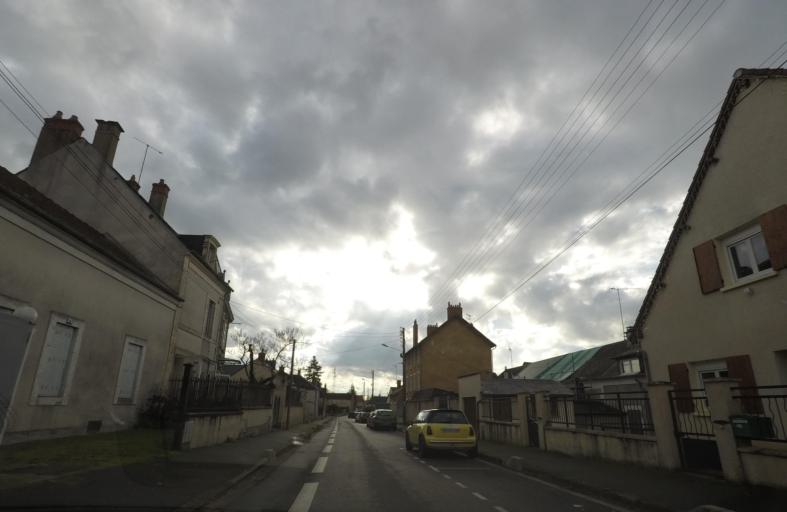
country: FR
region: Centre
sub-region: Departement du Cher
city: Bourges
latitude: 47.0691
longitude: 2.3990
